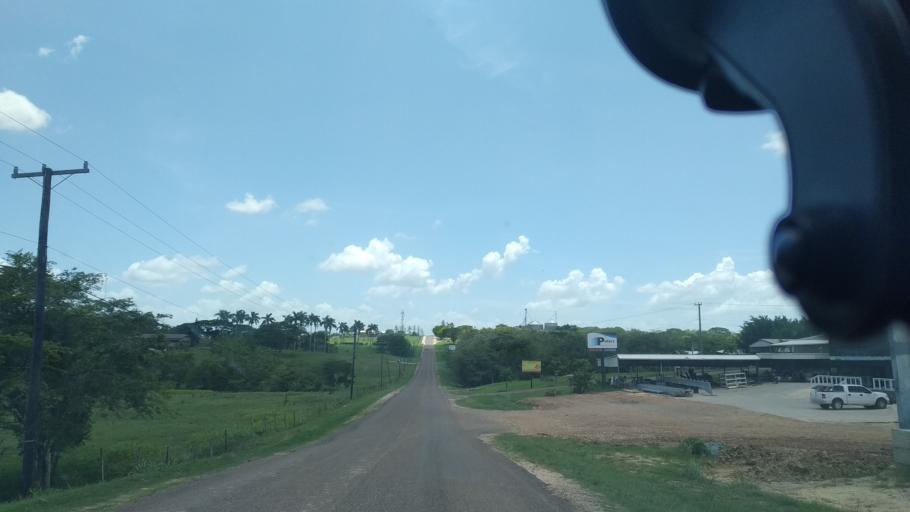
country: BZ
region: Cayo
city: San Ignacio
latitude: 17.2566
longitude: -88.9923
